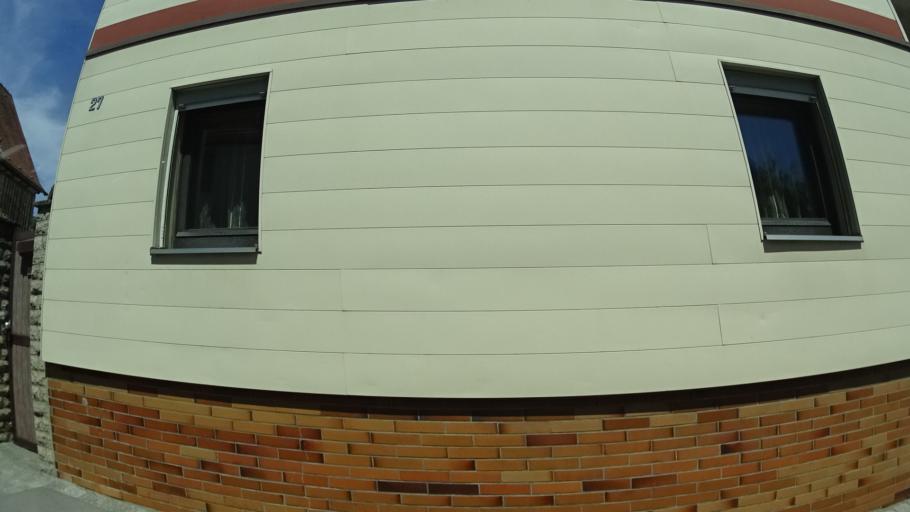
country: DE
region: Bavaria
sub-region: Regierungsbezirk Unterfranken
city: Euerbach
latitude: 50.0621
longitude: 10.1318
